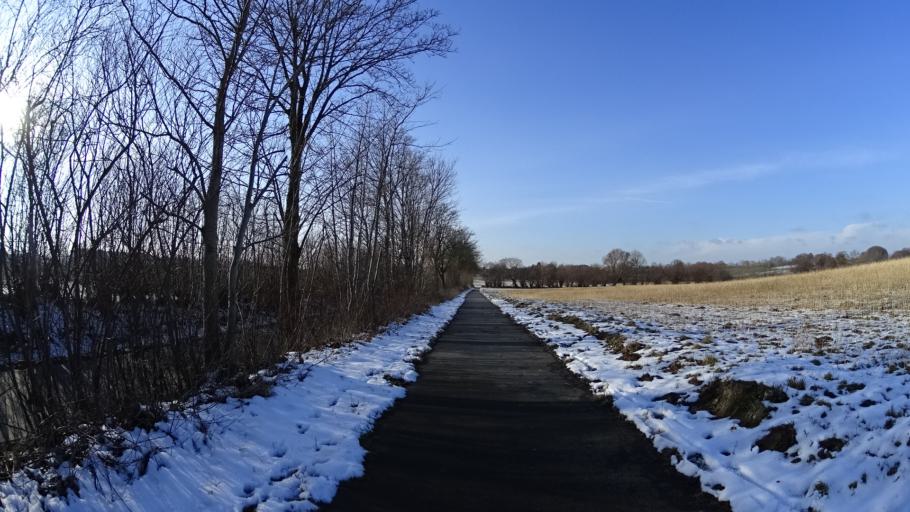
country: DE
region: Schleswig-Holstein
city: Martensrade
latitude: 54.2823
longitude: 10.3907
